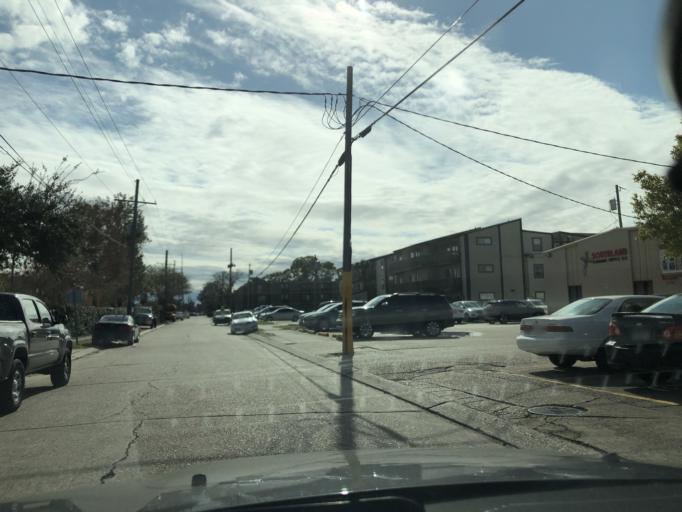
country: US
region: Louisiana
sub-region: Jefferson Parish
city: Metairie
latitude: 29.9951
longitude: -90.1610
